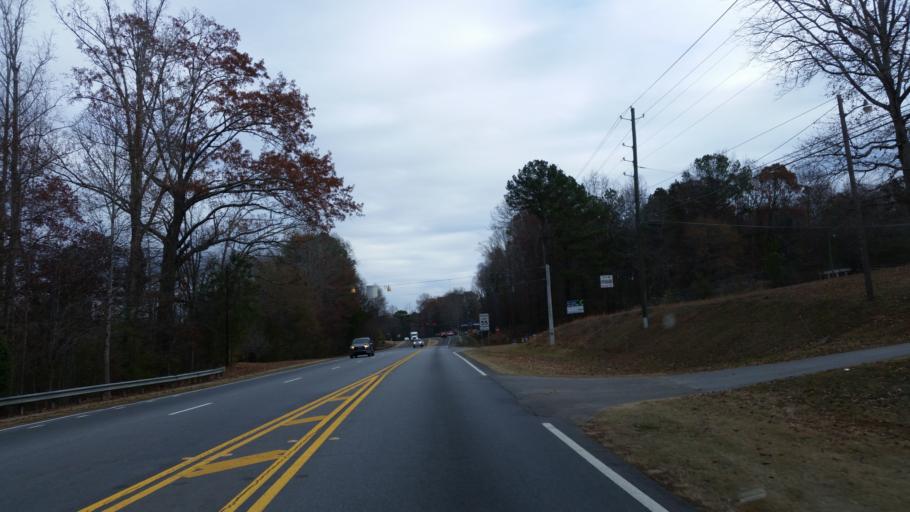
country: US
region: Georgia
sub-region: Cherokee County
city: Canton
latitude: 34.2134
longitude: -84.5313
